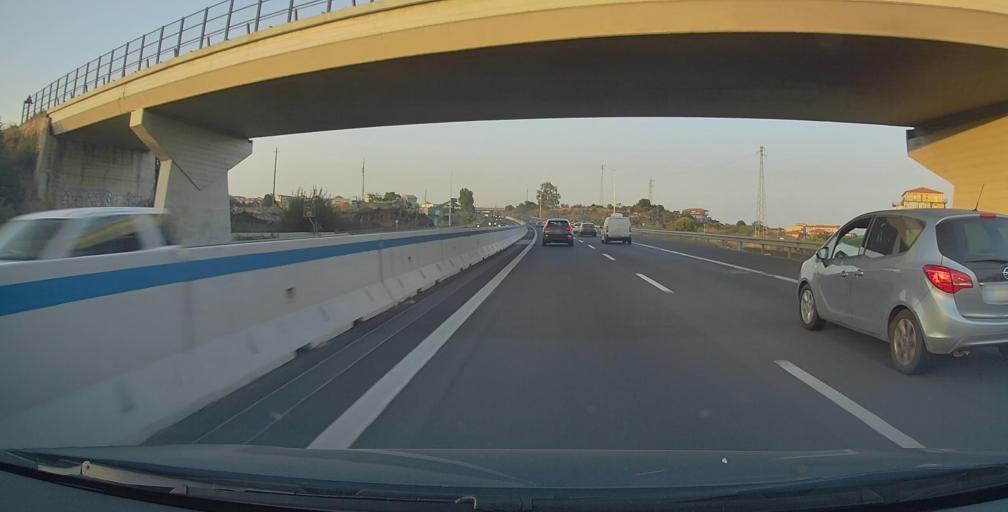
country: IT
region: Sicily
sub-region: Catania
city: Misterbianco
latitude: 37.5296
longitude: 15.0357
